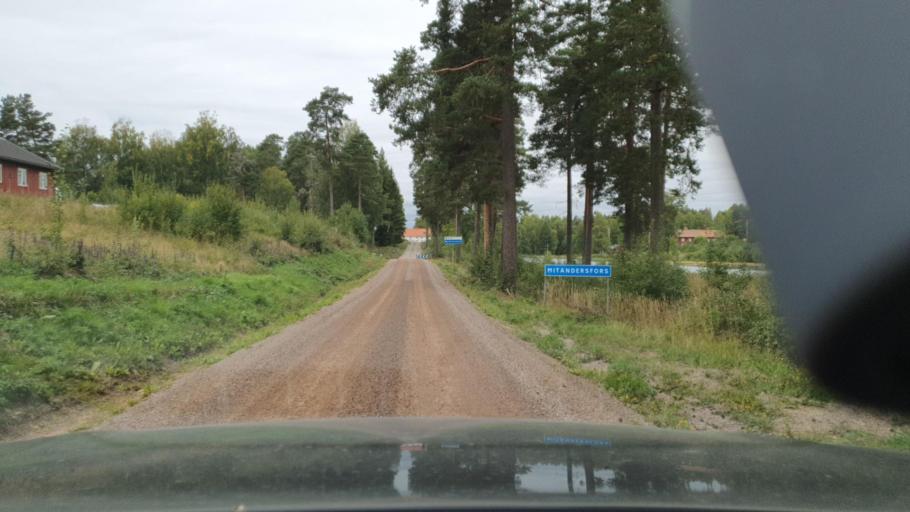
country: SE
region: Vaermland
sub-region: Eda Kommun
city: Charlottenberg
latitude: 60.0877
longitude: 12.5160
